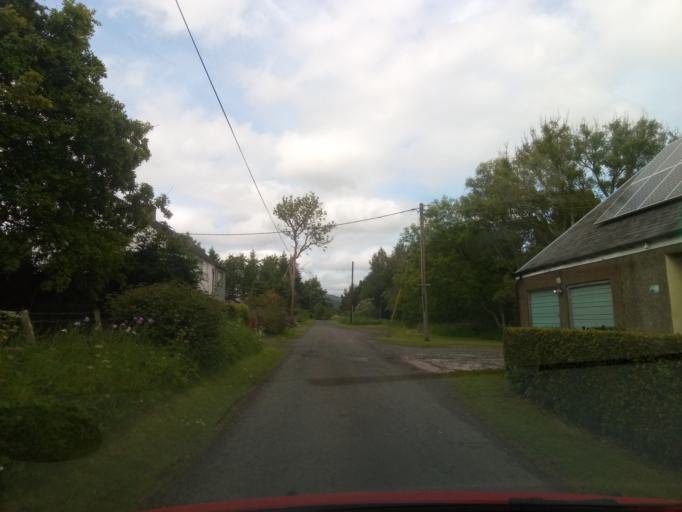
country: GB
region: Scotland
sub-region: The Scottish Borders
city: Selkirk
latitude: 55.5297
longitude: -2.8718
